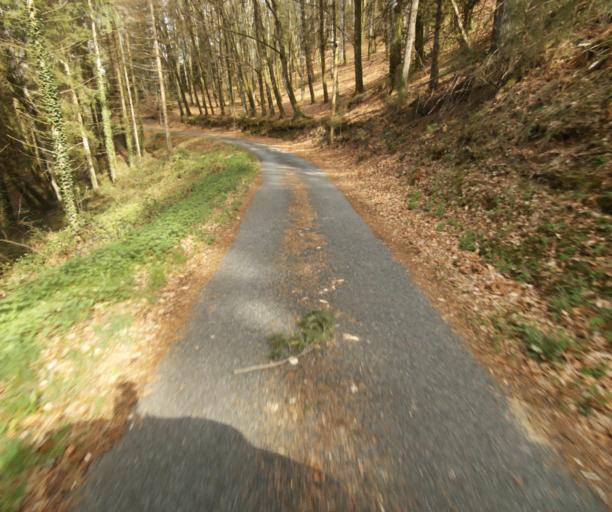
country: FR
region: Limousin
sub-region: Departement de la Correze
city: Correze
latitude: 45.3561
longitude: 1.8791
